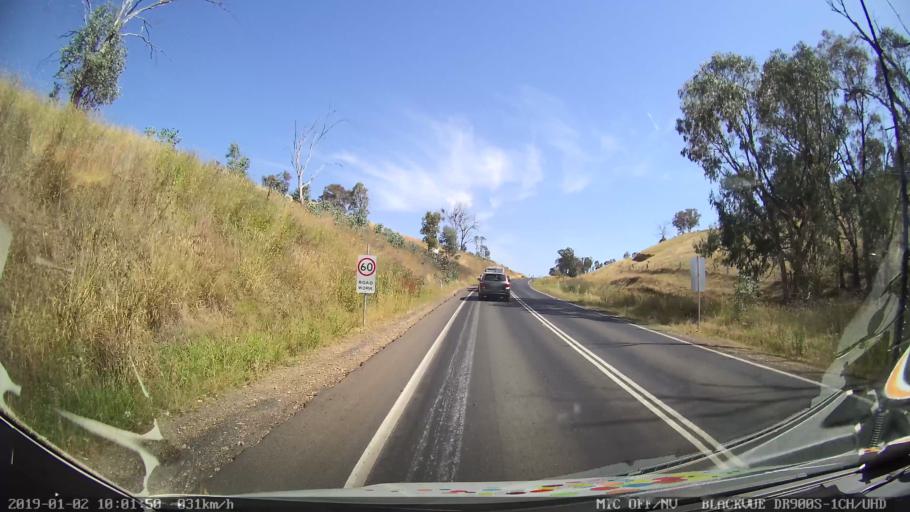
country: AU
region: New South Wales
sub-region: Gundagai
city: Gundagai
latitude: -35.1852
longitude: 148.1268
